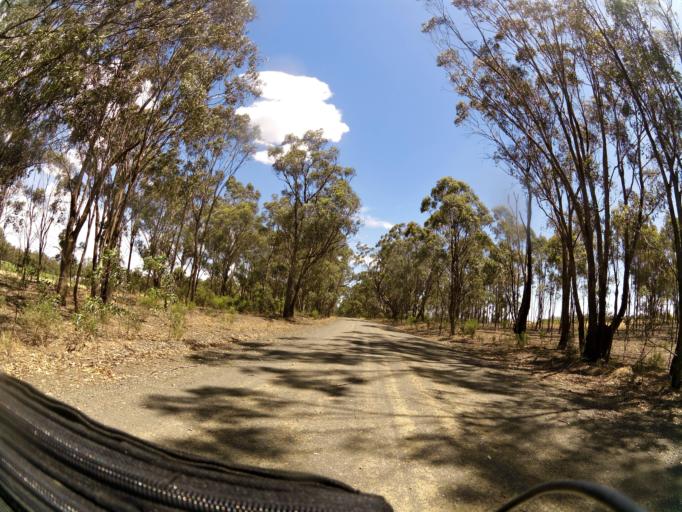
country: AU
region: Victoria
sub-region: Campaspe
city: Kyabram
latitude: -36.7973
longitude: 145.0803
